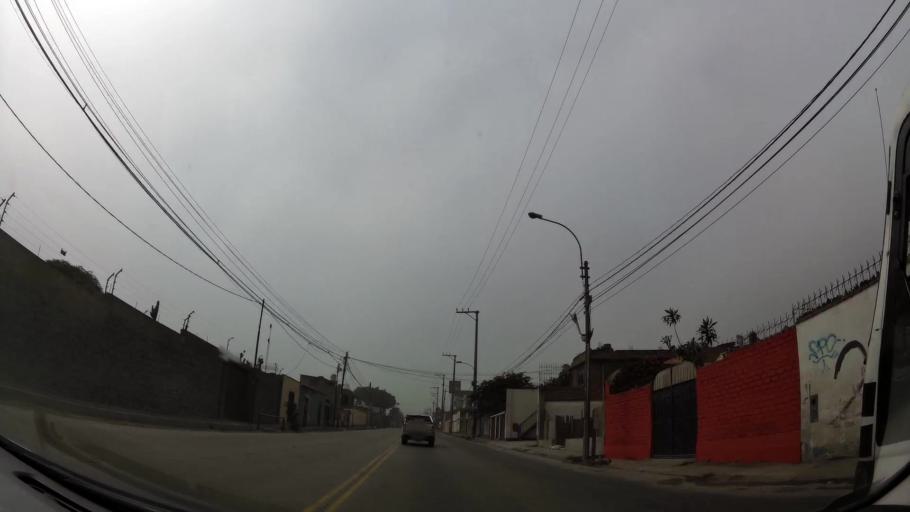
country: PE
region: Lima
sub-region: Lima
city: Chaclacayo
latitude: -11.9715
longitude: -76.7549
